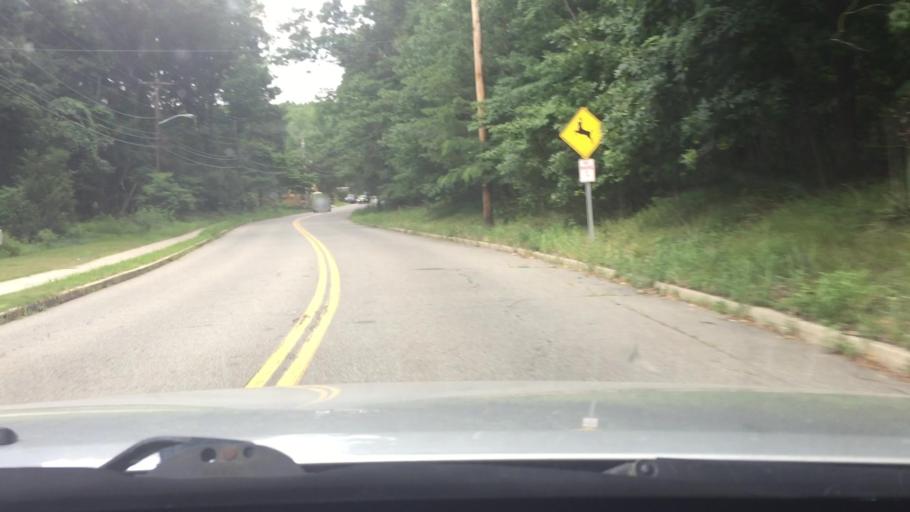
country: US
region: New Jersey
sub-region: Middlesex County
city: Spotswood
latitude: 40.4077
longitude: -74.4055
